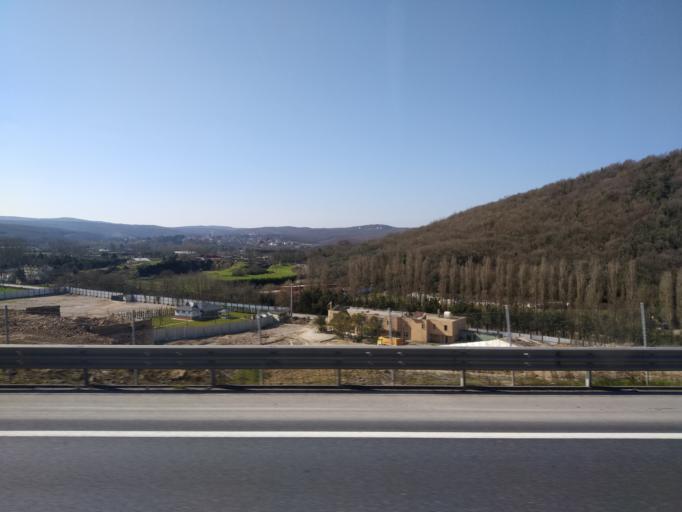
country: TR
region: Istanbul
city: Mahmut Sevket Pasa
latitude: 41.1349
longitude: 29.2867
